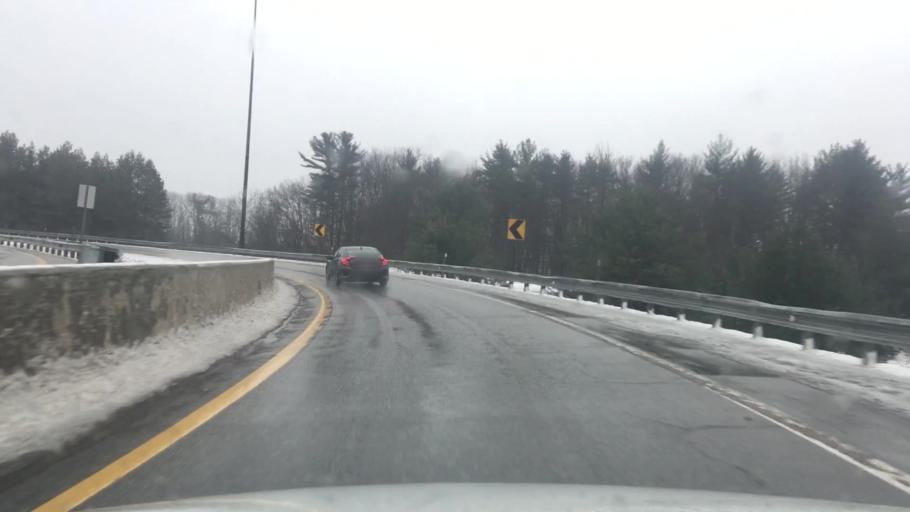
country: US
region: Maine
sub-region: York County
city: Saco
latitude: 43.5290
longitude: -70.4545
